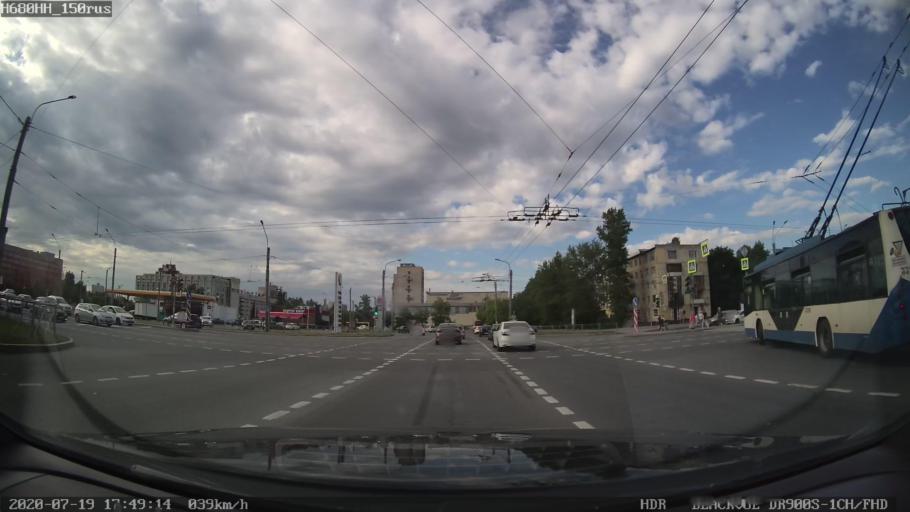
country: RU
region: St.-Petersburg
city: Avtovo
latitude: 59.8516
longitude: 30.3066
